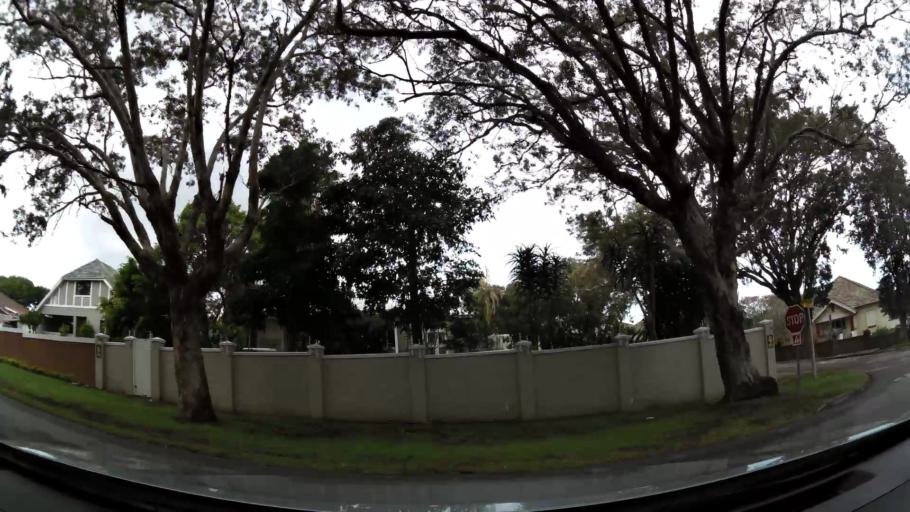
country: ZA
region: Eastern Cape
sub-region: Nelson Mandela Bay Metropolitan Municipality
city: Port Elizabeth
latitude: -33.9659
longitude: 25.5918
